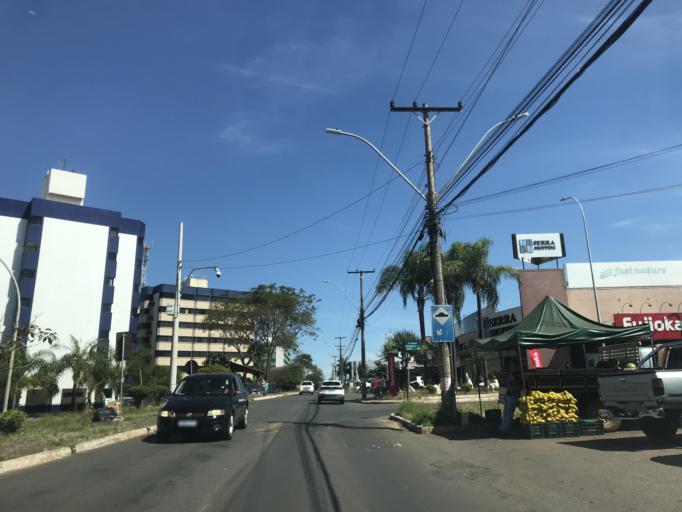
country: BR
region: Federal District
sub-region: Brasilia
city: Brasilia
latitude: -15.6519
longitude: -47.7898
